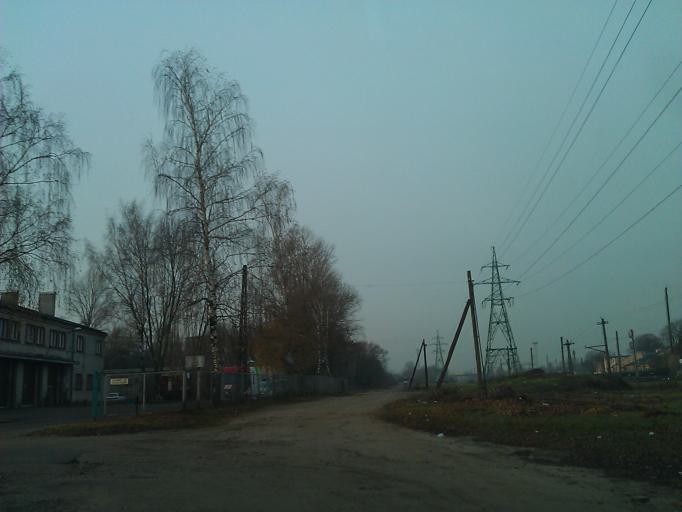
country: LV
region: Riga
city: Jaunciems
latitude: 56.9821
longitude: 24.1807
